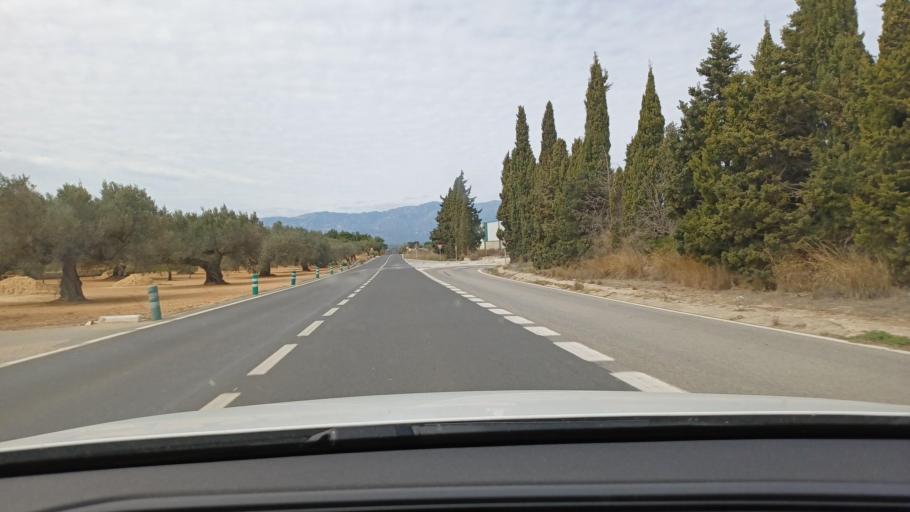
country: ES
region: Catalonia
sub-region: Provincia de Tarragona
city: Masdenverge
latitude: 40.7089
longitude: 0.5415
